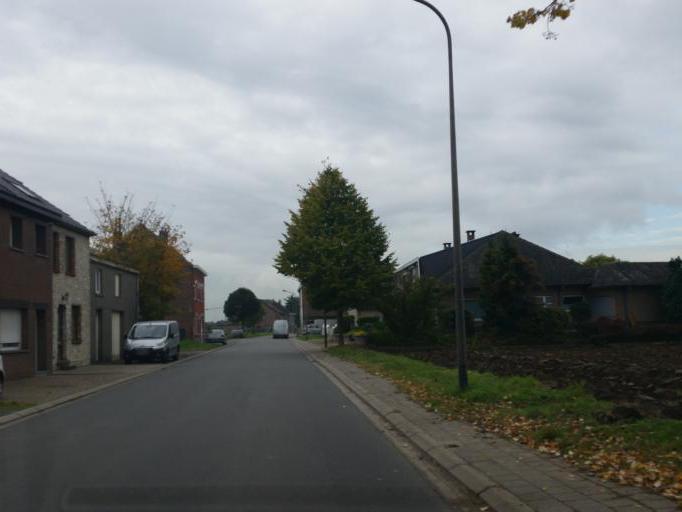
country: BE
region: Flanders
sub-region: Provincie Vlaams-Brabant
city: Steenokkerzeel
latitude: 50.9172
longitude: 4.4885
